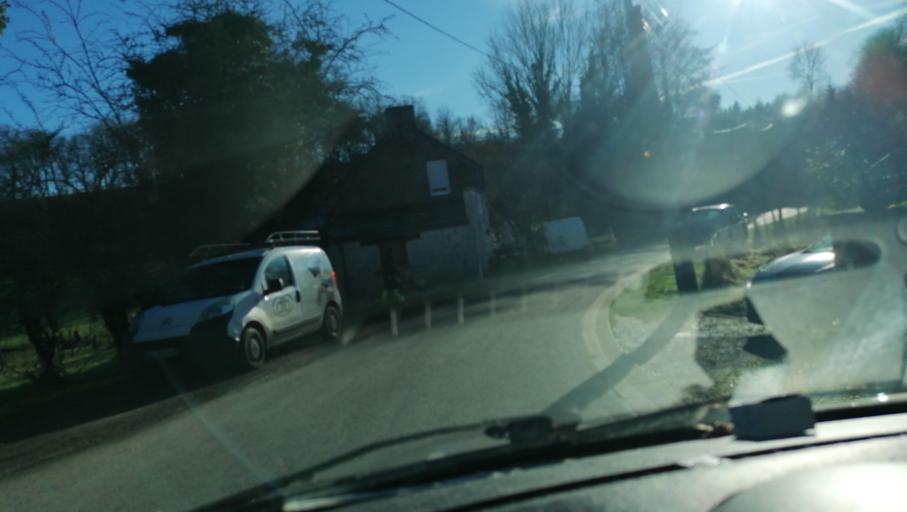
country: FR
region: Nord-Pas-de-Calais
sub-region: Departement du Nord
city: Marpent
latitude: 50.2055
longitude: 4.0755
